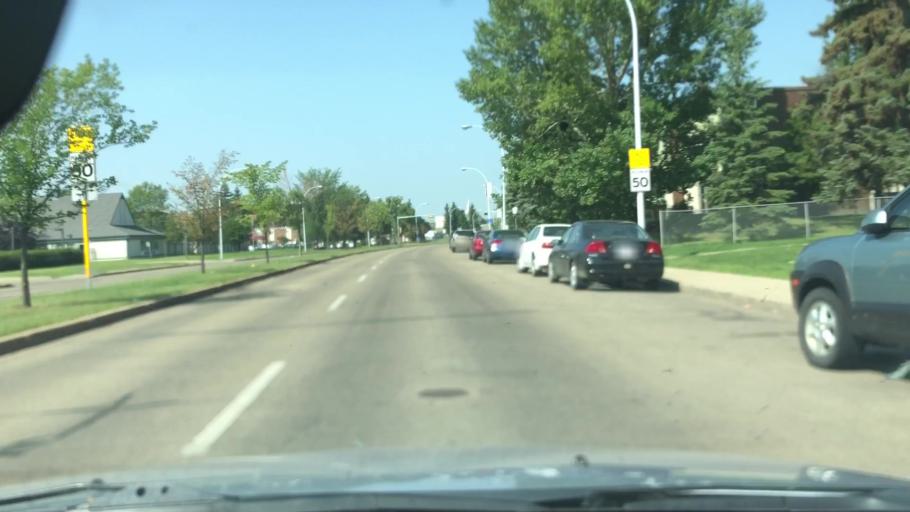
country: CA
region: Alberta
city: Edmonton
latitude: 53.6058
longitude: -113.4797
